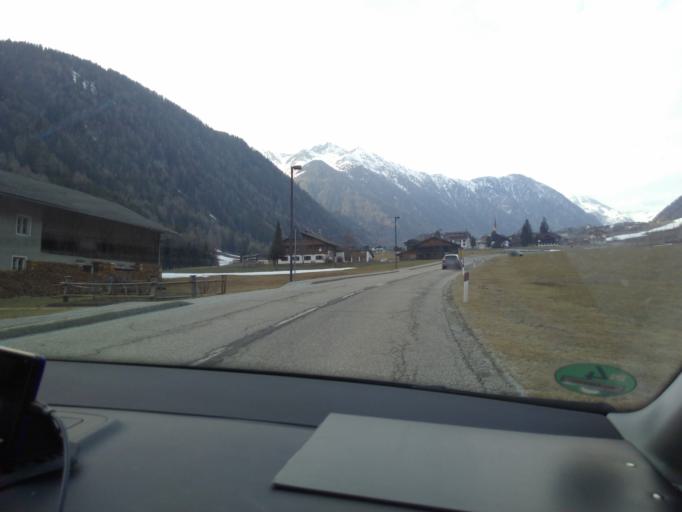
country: IT
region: Trentino-Alto Adige
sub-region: Bolzano
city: Fortezza
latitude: 46.8312
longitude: 11.6316
